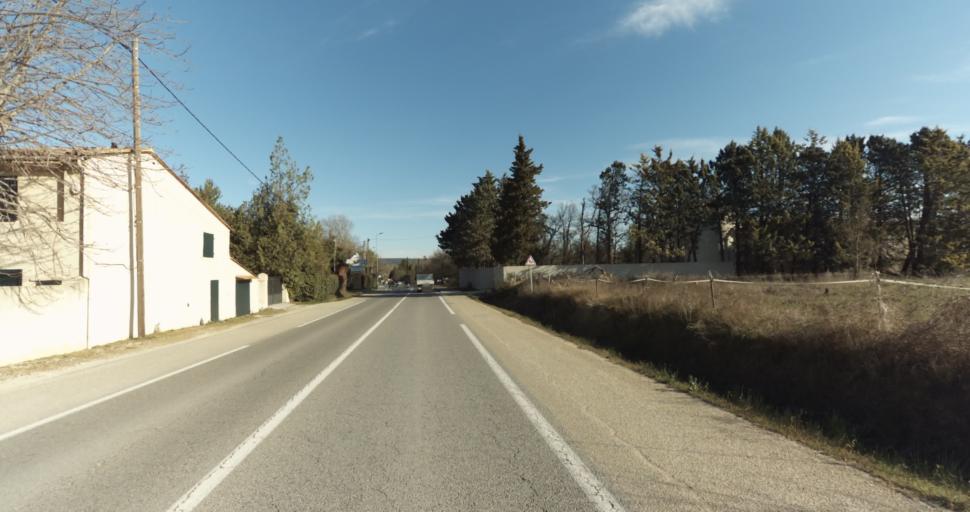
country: FR
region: Provence-Alpes-Cote d'Azur
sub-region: Departement des Bouches-du-Rhone
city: Aix-en-Provence
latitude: 43.5713
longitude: 5.4330
